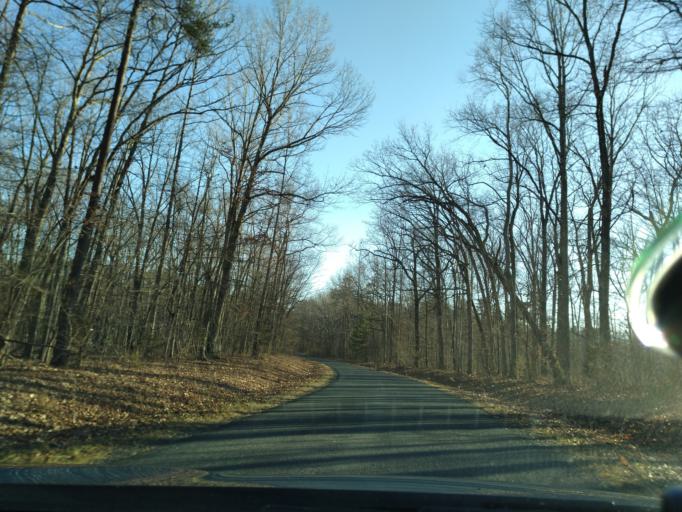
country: US
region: Virginia
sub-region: Appomattox County
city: Appomattox
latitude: 37.3936
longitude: -78.6583
